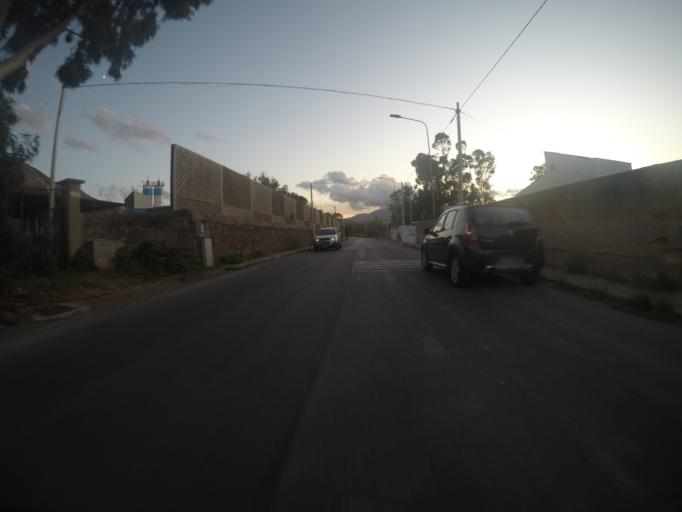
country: IT
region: Sicily
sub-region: Palermo
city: Isola delle Femmine
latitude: 38.1832
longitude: 13.2413
